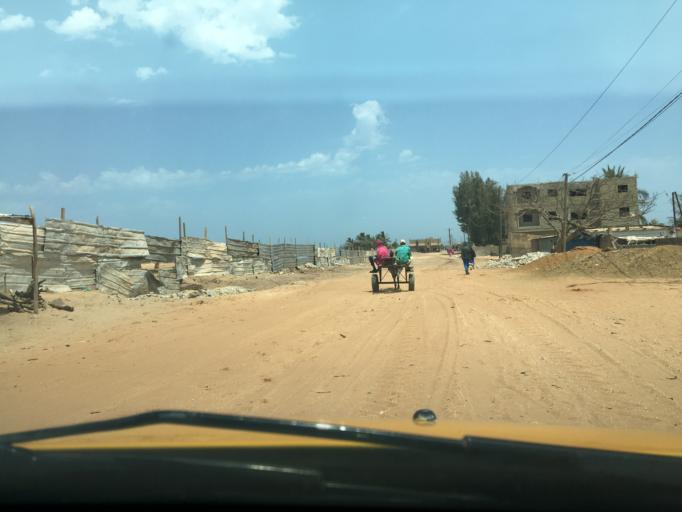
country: SN
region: Thies
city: Thies
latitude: 14.8050
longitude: -17.1864
